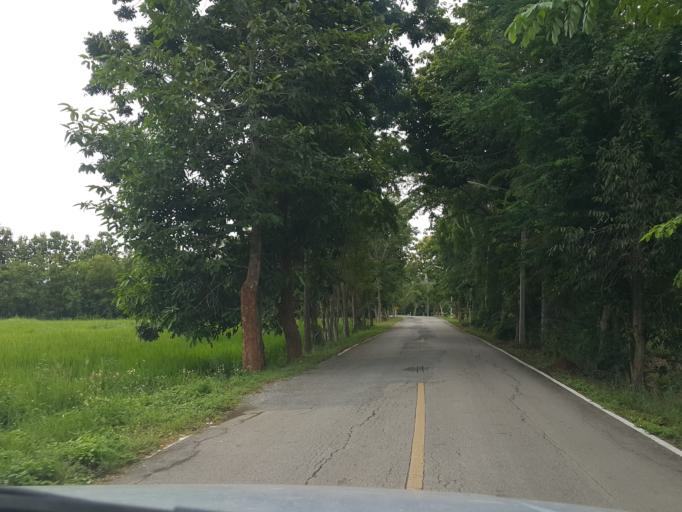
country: TH
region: Chiang Mai
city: San Kamphaeng
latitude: 18.8061
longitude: 99.1419
